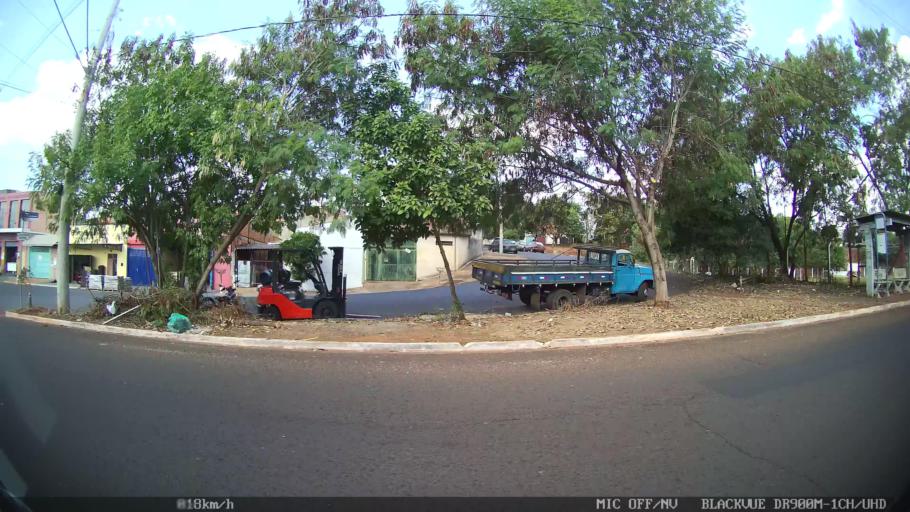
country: BR
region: Sao Paulo
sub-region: Ribeirao Preto
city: Ribeirao Preto
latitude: -21.1917
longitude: -47.8450
